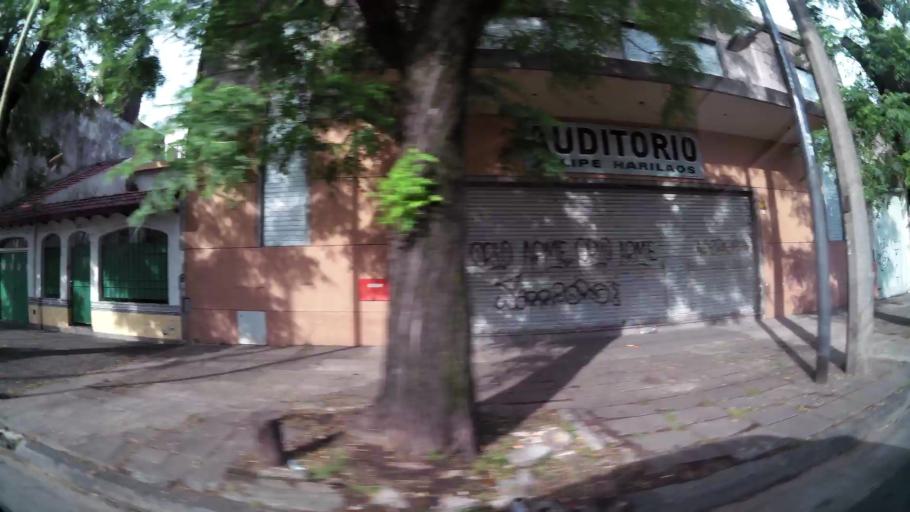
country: AR
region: Buenos Aires F.D.
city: Villa Lugano
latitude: -34.6460
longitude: -58.4590
